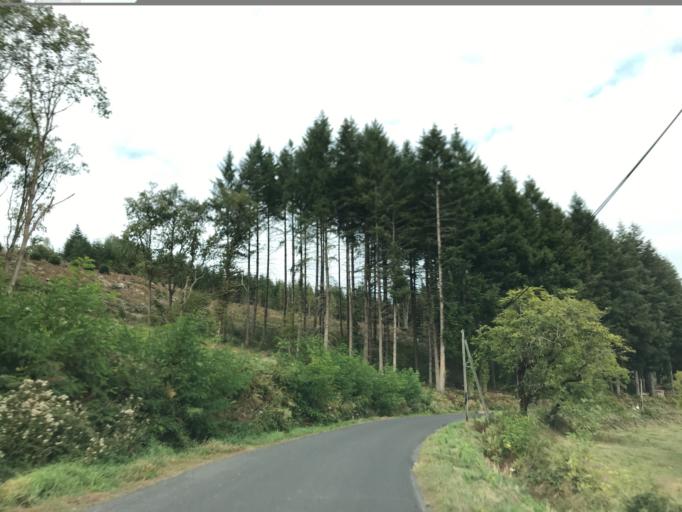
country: FR
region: Auvergne
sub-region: Departement du Puy-de-Dome
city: Celles-sur-Durolle
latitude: 45.8238
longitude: 3.6218
